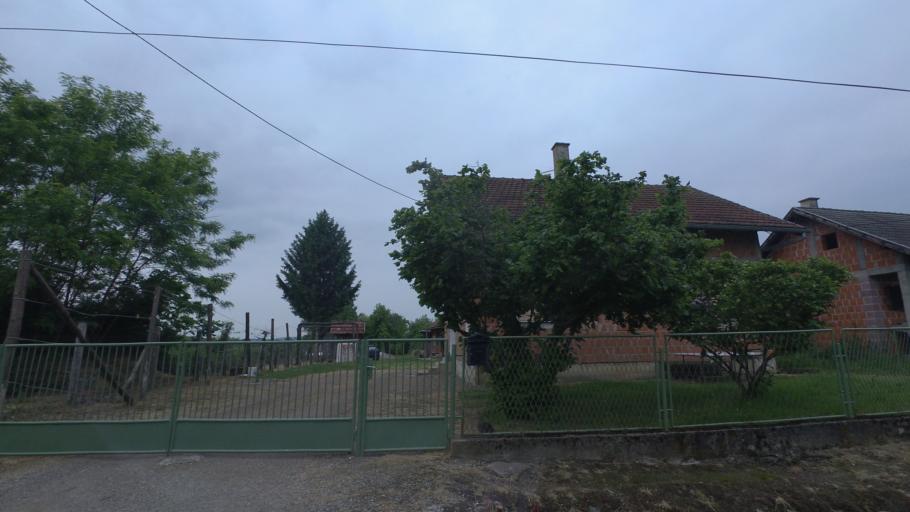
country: HR
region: Sisacko-Moslavacka
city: Gvozd
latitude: 45.2763
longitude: 15.9584
